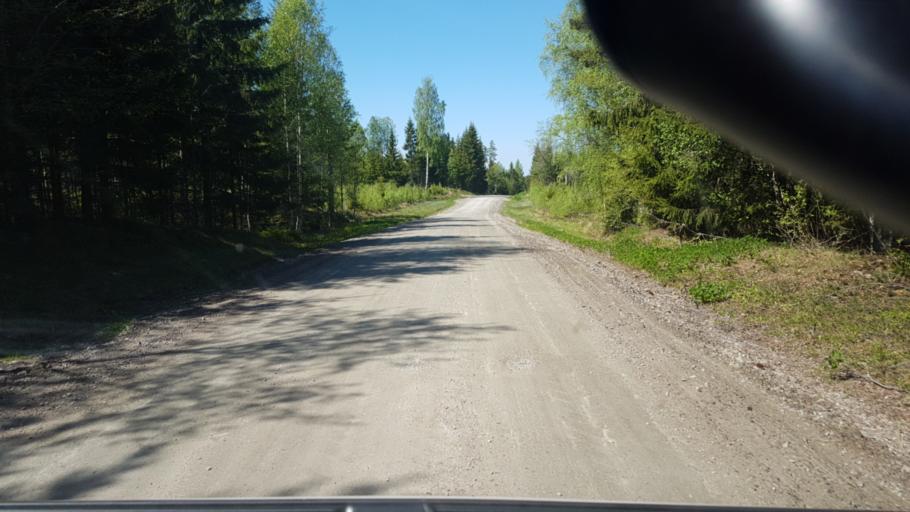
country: SE
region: Vaermland
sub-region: Arvika Kommun
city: Arvika
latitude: 59.8817
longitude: 12.6808
